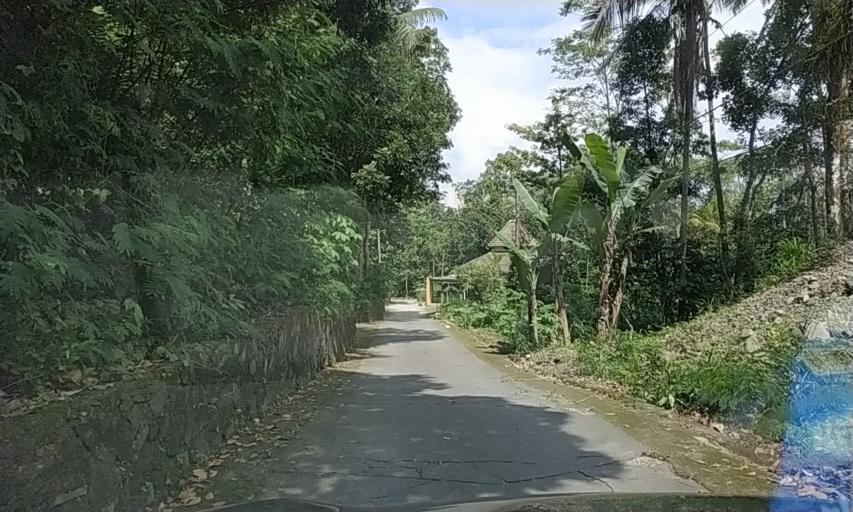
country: ID
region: Central Java
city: Jogonalan
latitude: -7.6317
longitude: 110.4825
